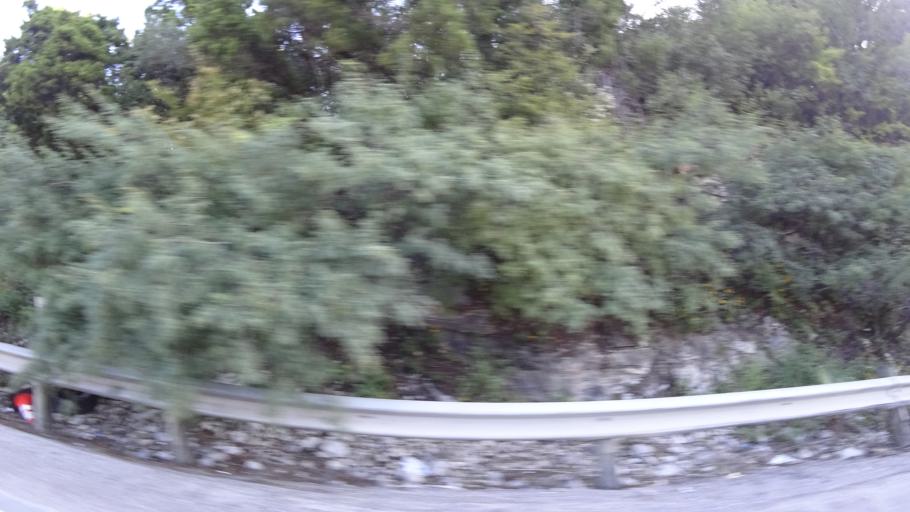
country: US
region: Texas
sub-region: Travis County
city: Rollingwood
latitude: 30.2722
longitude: -97.7971
